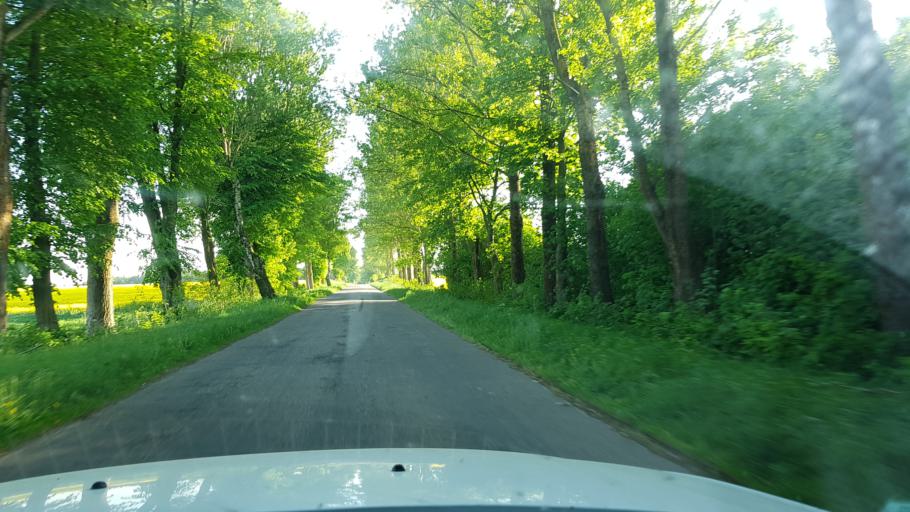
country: PL
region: West Pomeranian Voivodeship
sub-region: Powiat lobeski
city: Dobra
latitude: 53.6273
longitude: 15.3556
